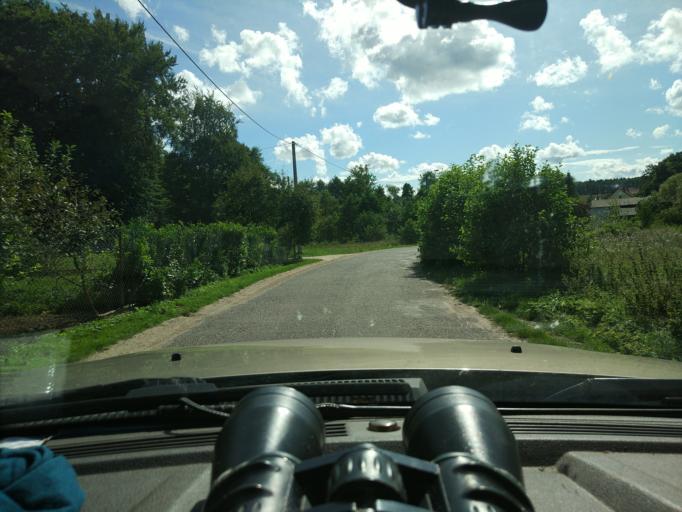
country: PL
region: Pomeranian Voivodeship
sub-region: Powiat wejherowski
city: Choczewo
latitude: 54.7579
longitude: 17.7923
